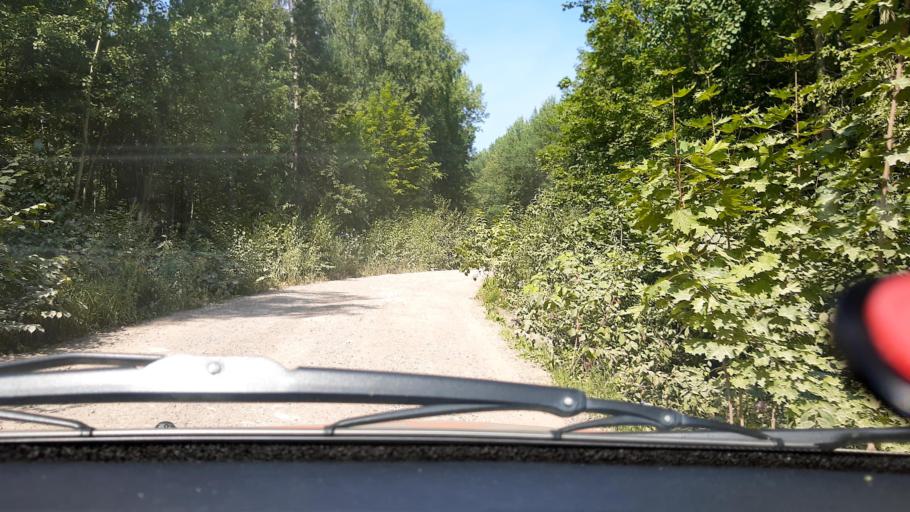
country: RU
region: Bashkortostan
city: Karmaskaly
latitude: 54.3865
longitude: 55.8920
